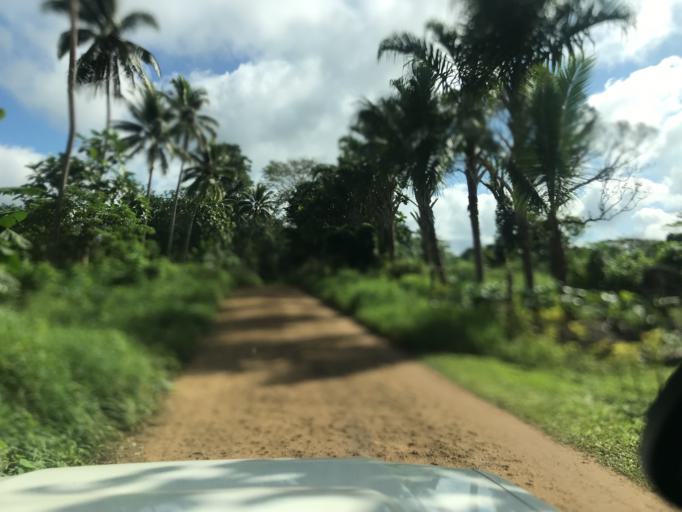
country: VU
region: Sanma
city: Luganville
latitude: -15.4803
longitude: 167.0890
